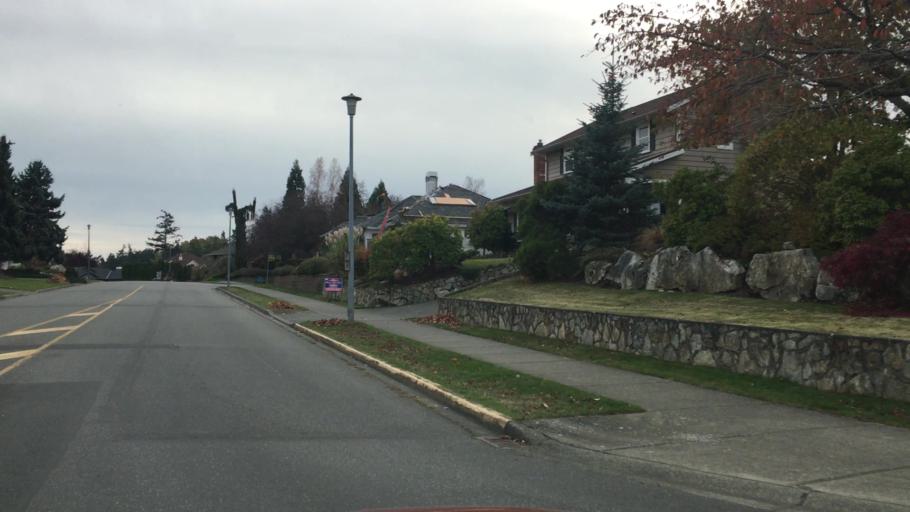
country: CA
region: British Columbia
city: Victoria
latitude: 48.5045
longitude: -123.3605
